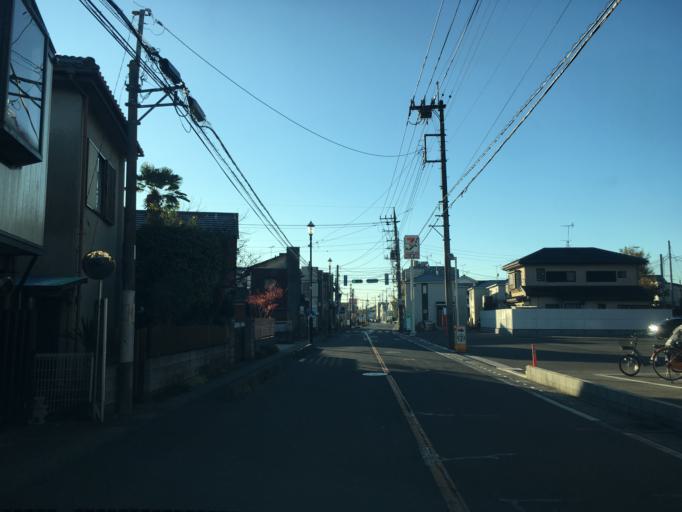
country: JP
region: Saitama
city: Sayama
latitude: 35.8065
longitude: 139.4178
